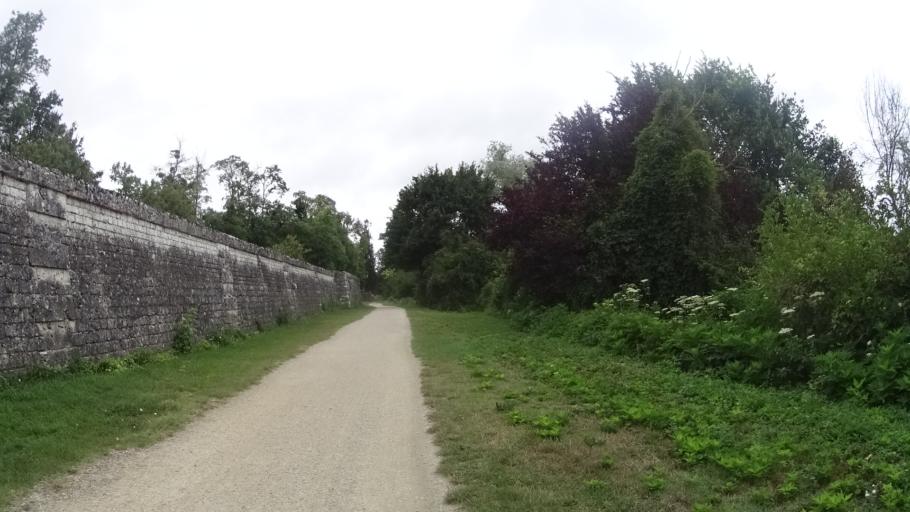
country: FR
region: Centre
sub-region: Departement du Loir-et-Cher
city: Saint-Claude-de-Diray
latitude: 47.6423
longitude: 1.4173
